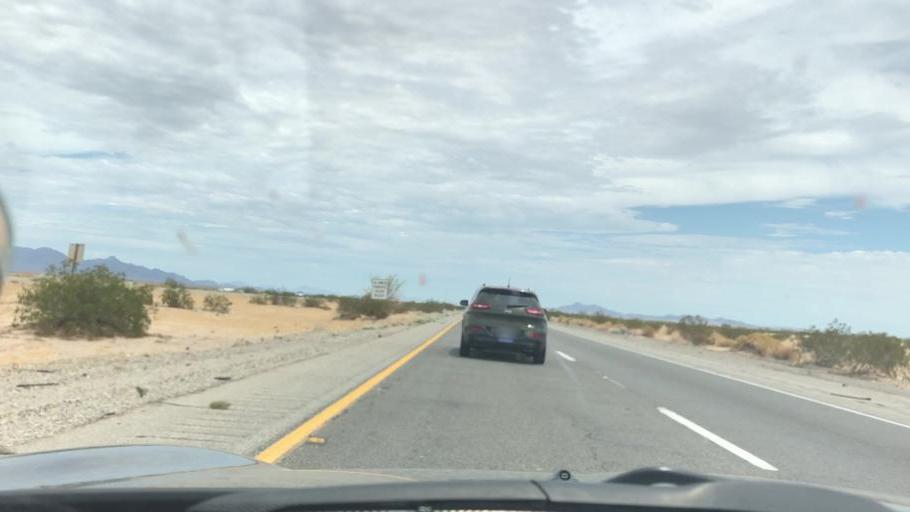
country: US
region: California
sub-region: Riverside County
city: Mesa Verde
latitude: 33.6294
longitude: -115.0701
